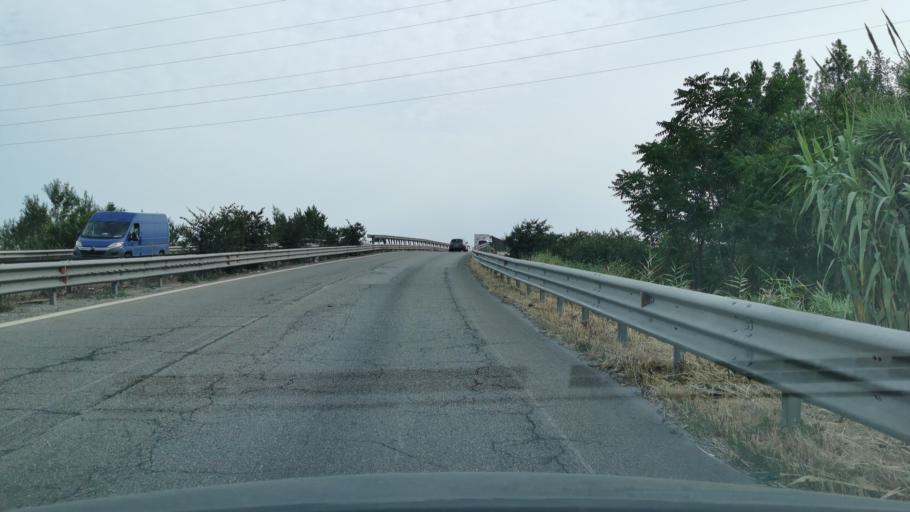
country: IT
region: Emilia-Romagna
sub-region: Provincia di Modena
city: Modena
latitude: 44.6440
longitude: 10.9611
